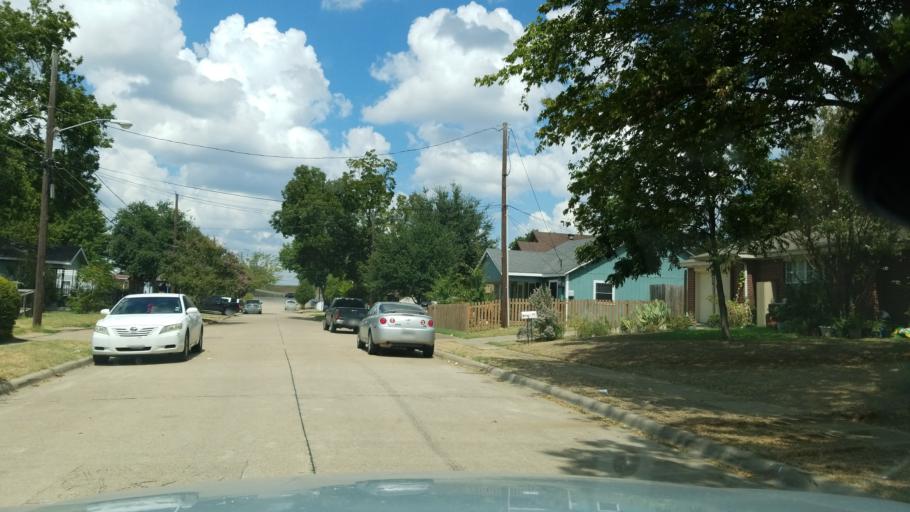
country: US
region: Texas
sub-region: Dallas County
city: Dallas
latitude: 32.7822
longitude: -96.8320
